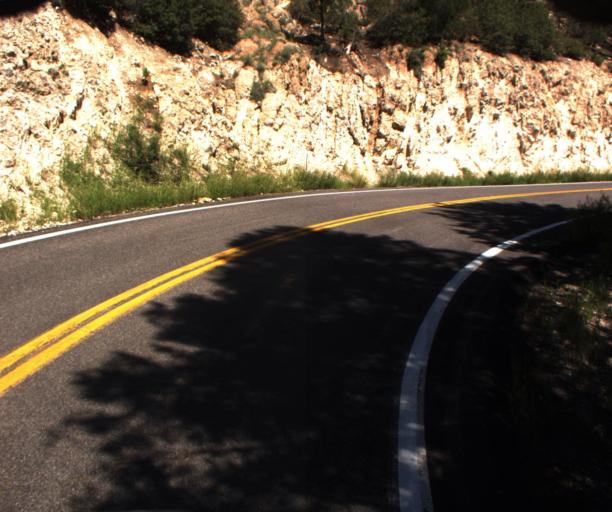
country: US
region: Arizona
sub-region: Greenlee County
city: Morenci
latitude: 33.1867
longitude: -109.3858
